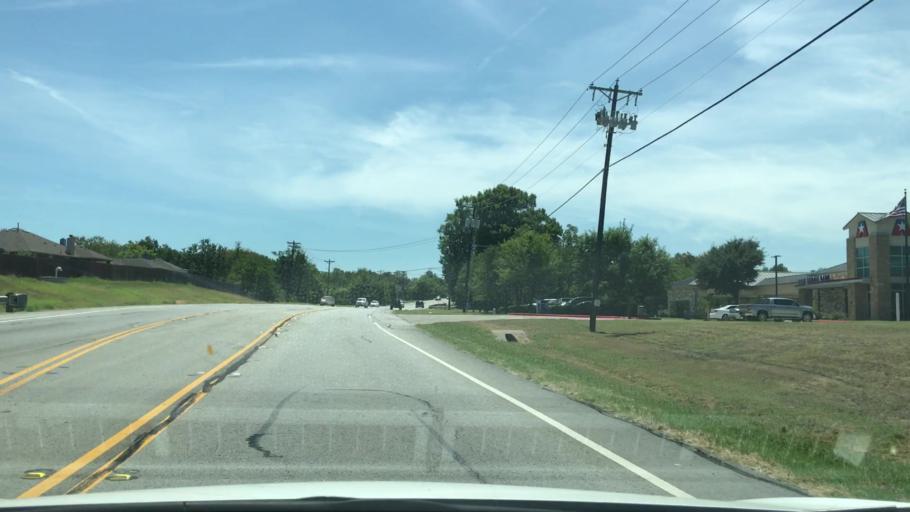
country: US
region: Texas
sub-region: Rockwall County
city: Rockwall
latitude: 32.9427
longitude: -96.4604
